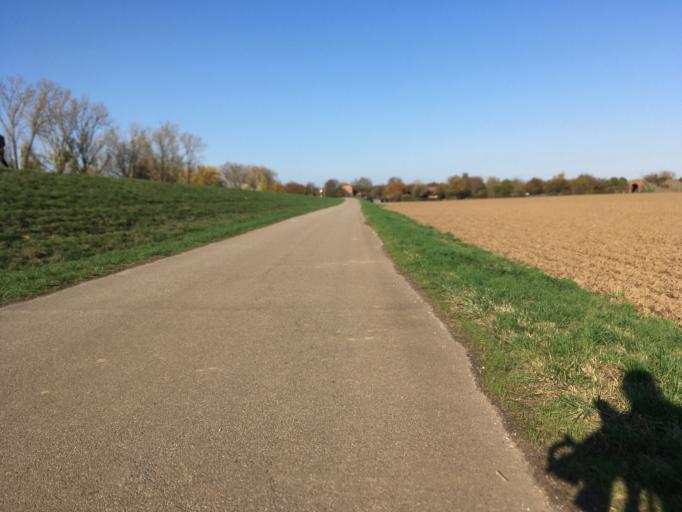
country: DE
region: Rheinland-Pfalz
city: Worms
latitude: 49.6477
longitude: 8.3844
